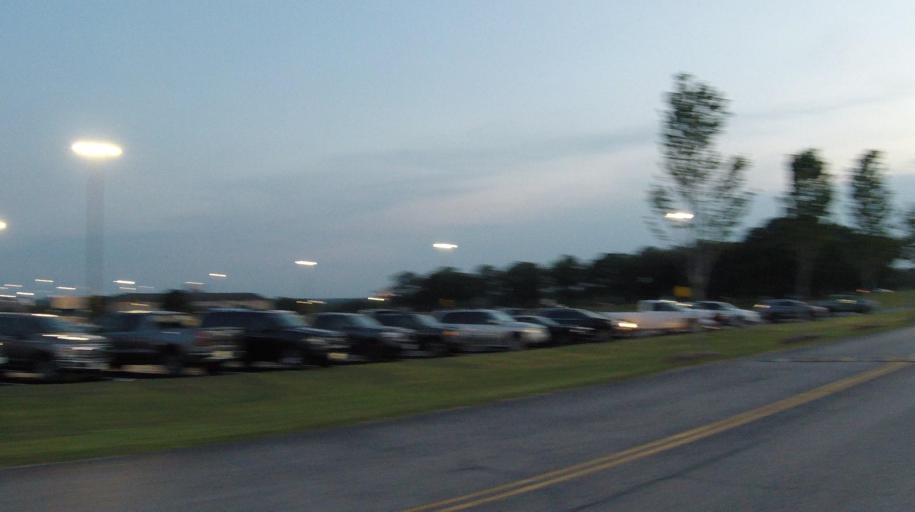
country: US
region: Texas
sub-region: Cooke County
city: Gainesville
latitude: 33.7552
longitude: -97.1317
